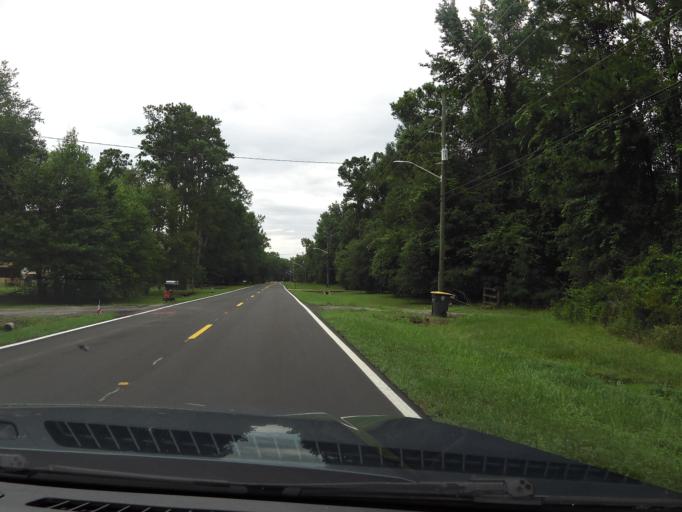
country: US
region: Florida
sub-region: Nassau County
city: Nassau Village-Ratliff
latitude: 30.4547
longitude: -81.7806
